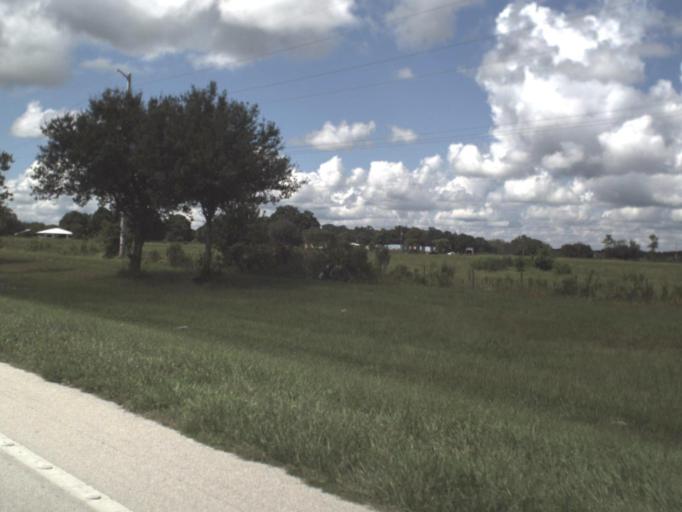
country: US
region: Florida
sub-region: DeSoto County
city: Southeast Arcadia
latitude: 27.2088
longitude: -81.7482
